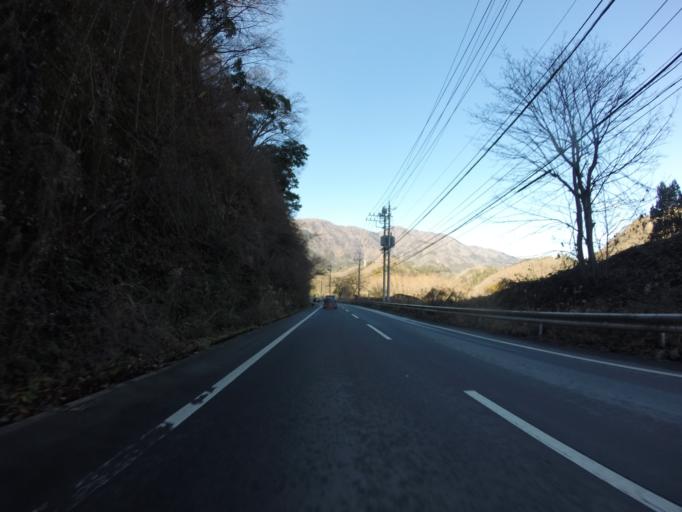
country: JP
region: Yamanashi
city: Ryuo
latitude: 35.4340
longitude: 138.4184
